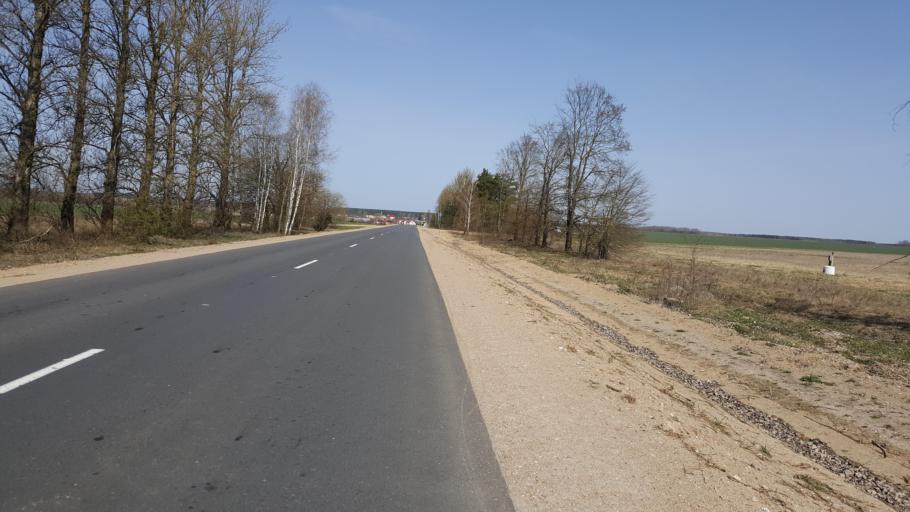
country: BY
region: Brest
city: Kamyanyets
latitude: 52.4561
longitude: 23.7353
